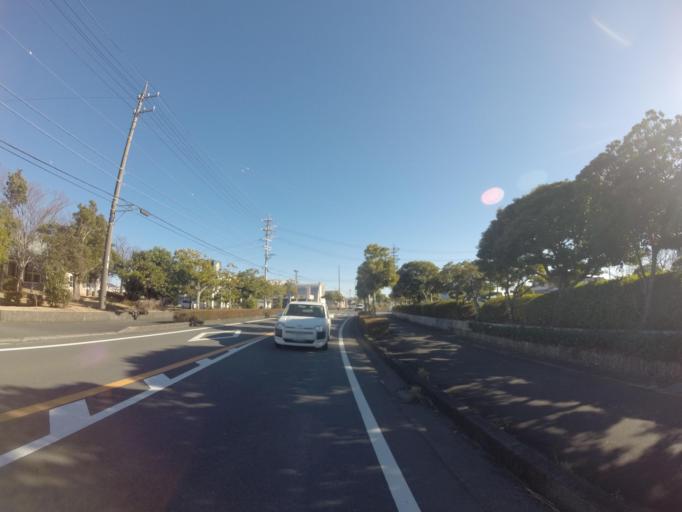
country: JP
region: Shizuoka
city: Fujieda
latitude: 34.8040
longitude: 138.2850
